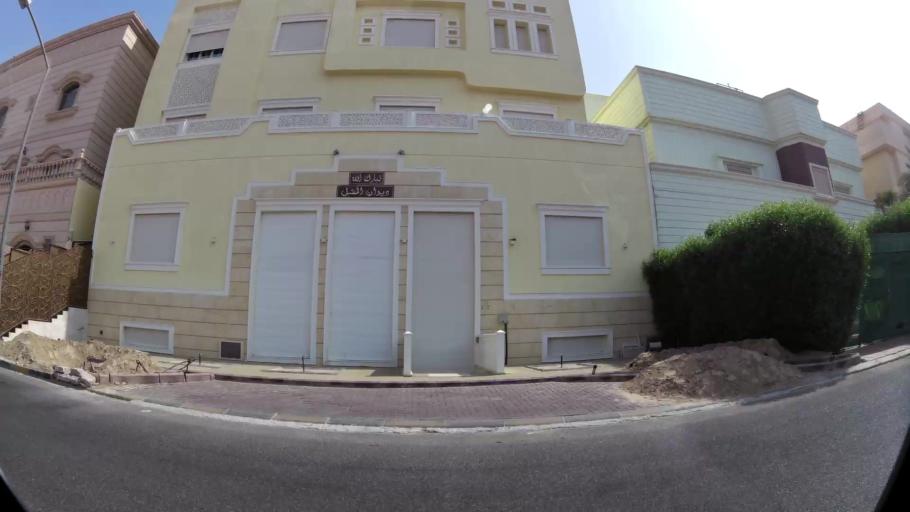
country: KW
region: Muhafazat al Jahra'
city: Al Jahra'
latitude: 29.3042
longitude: 47.7020
